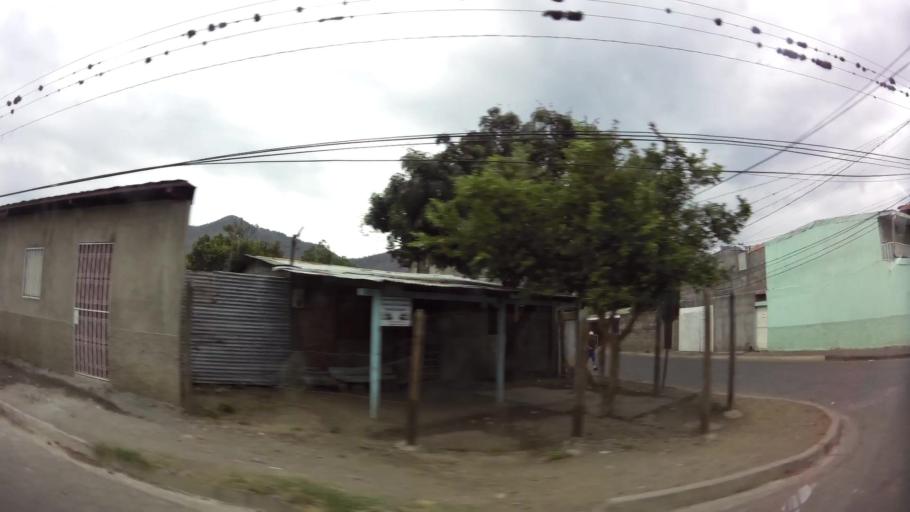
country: NI
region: Jinotega
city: Jinotega
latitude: 13.0959
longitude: -85.9992
